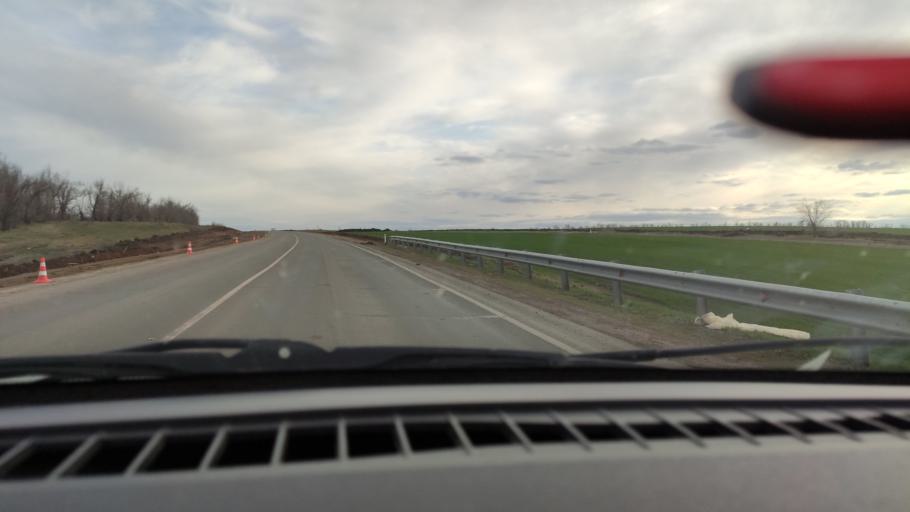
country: RU
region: Orenburg
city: Sakmara
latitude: 52.1855
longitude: 55.2951
